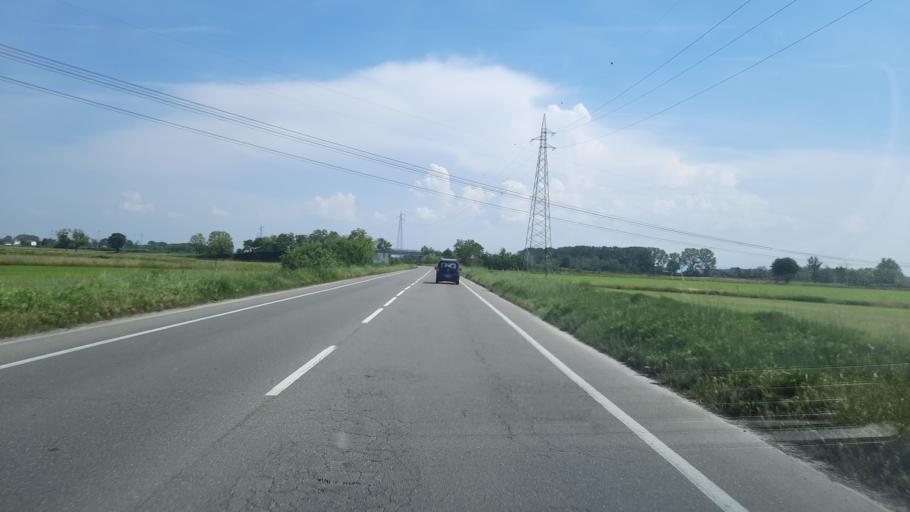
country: IT
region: Lombardy
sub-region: Provincia di Pavia
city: Gropello Cairoli
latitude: 45.1716
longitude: 8.9761
